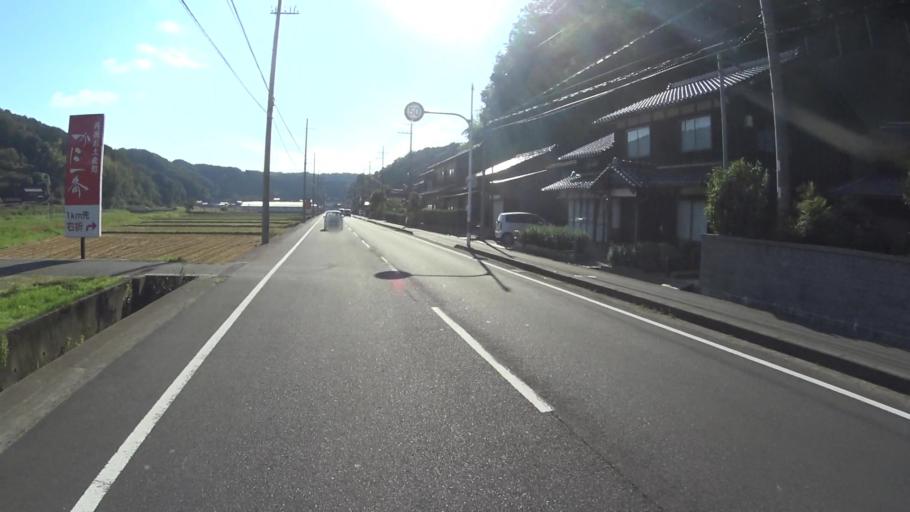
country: JP
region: Hyogo
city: Toyooka
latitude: 35.6537
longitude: 134.9816
